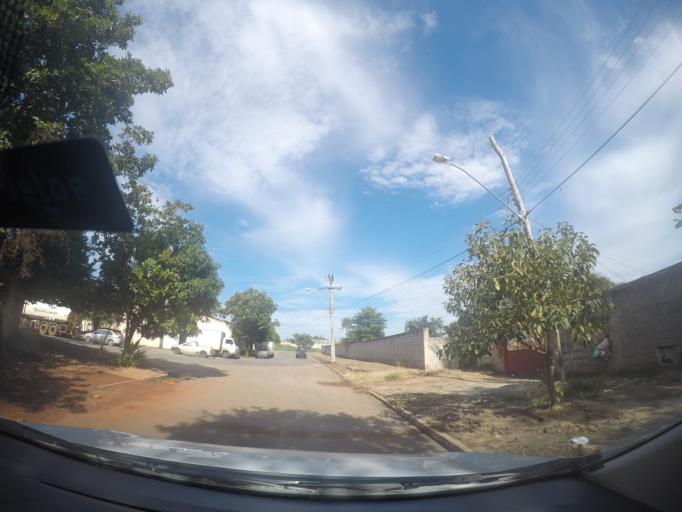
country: BR
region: Goias
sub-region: Goiania
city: Goiania
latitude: -16.6707
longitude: -49.2001
